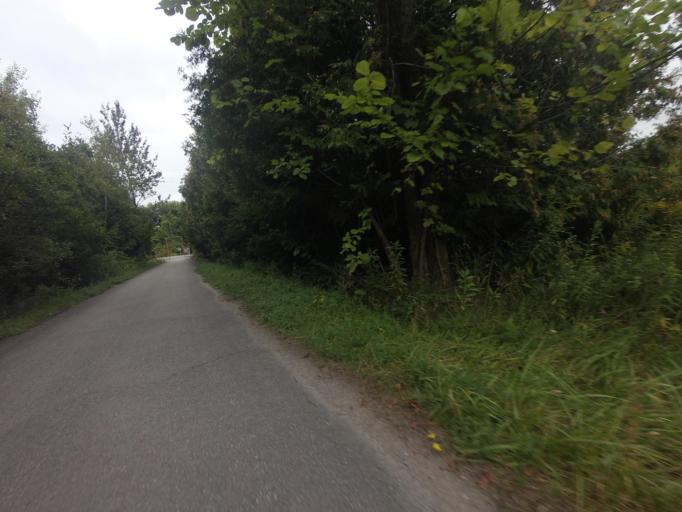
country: CA
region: Ontario
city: Omemee
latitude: 44.3805
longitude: -78.7512
